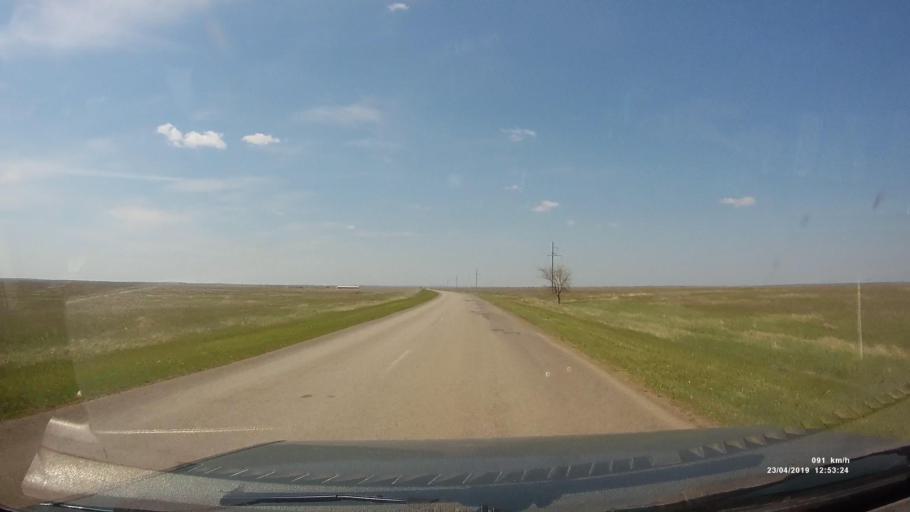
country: RU
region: Kalmykiya
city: Yashalta
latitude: 46.5735
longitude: 42.5965
